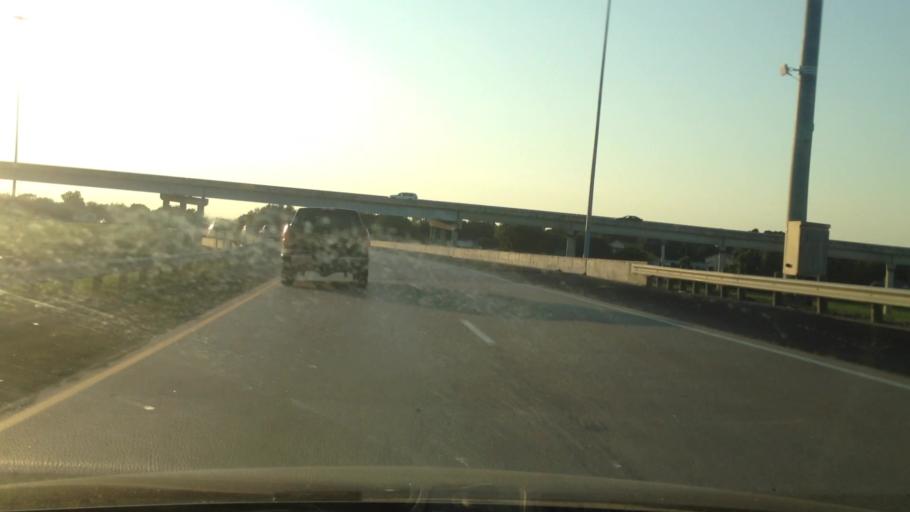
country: US
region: Texas
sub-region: Tarrant County
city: Kennedale
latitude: 32.6704
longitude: -97.2071
